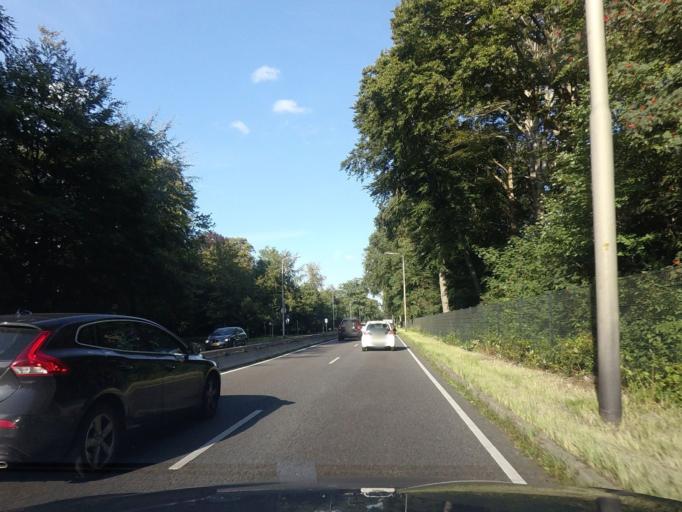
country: NL
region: South Holland
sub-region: Gemeente Wassenaar
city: Wassenaar
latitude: 52.1317
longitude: 4.3977
